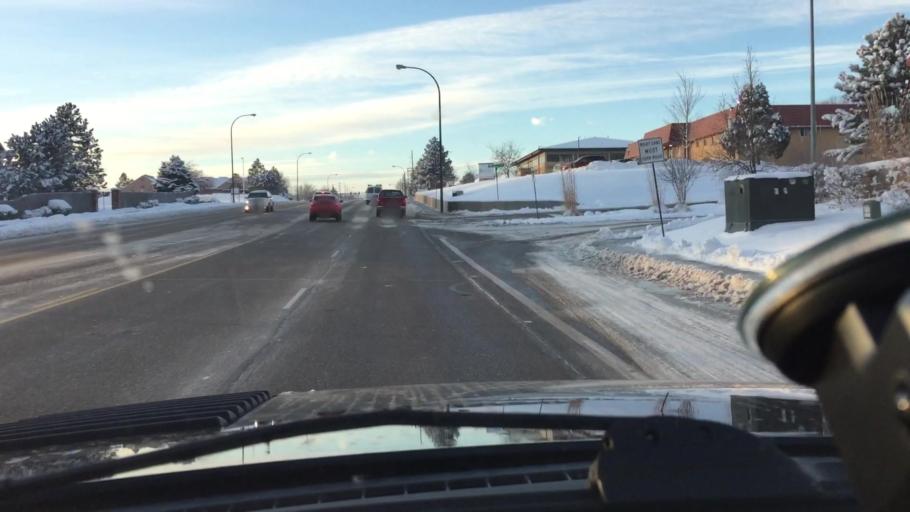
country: US
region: Colorado
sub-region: Adams County
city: Federal Heights
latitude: 39.8599
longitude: -104.9967
